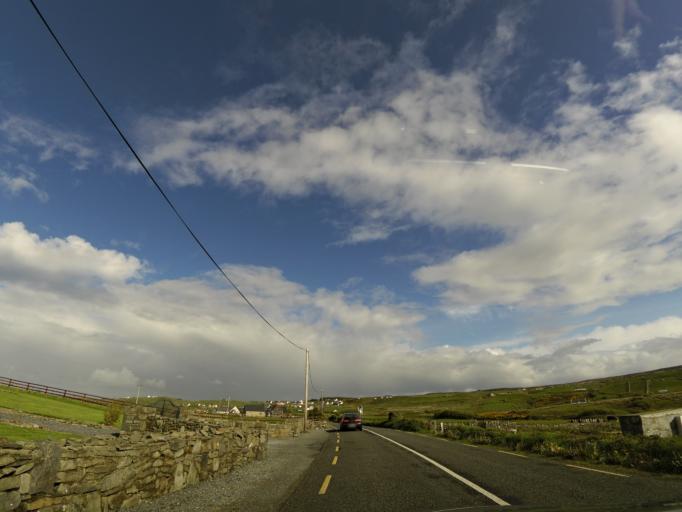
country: IE
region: Connaught
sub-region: County Galway
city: Bearna
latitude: 53.0133
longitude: -9.3713
